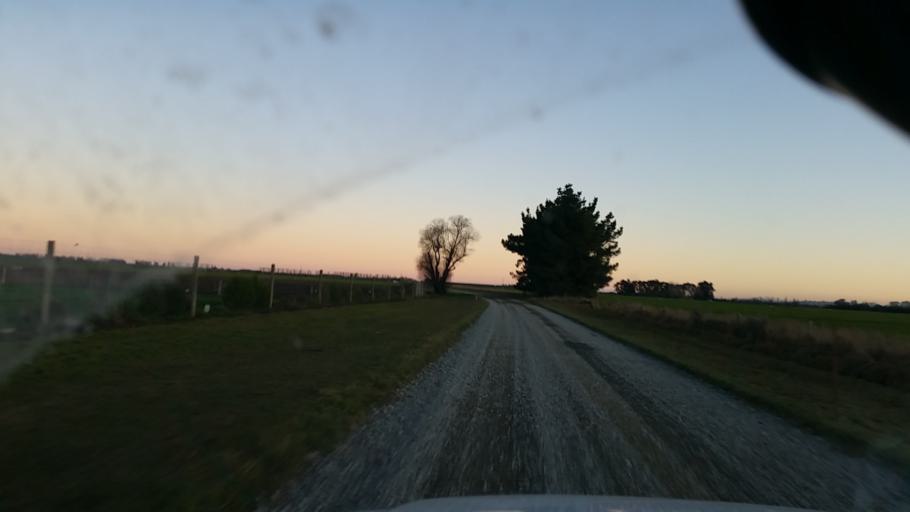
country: NZ
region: Canterbury
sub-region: Ashburton District
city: Tinwald
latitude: -44.0609
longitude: 171.6608
